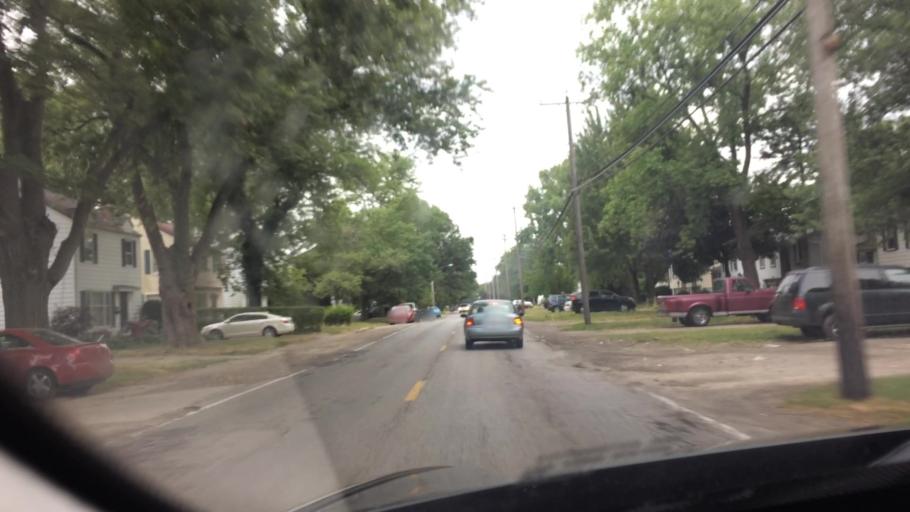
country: US
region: Ohio
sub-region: Lucas County
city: Ottawa Hills
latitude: 41.6449
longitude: -83.6406
